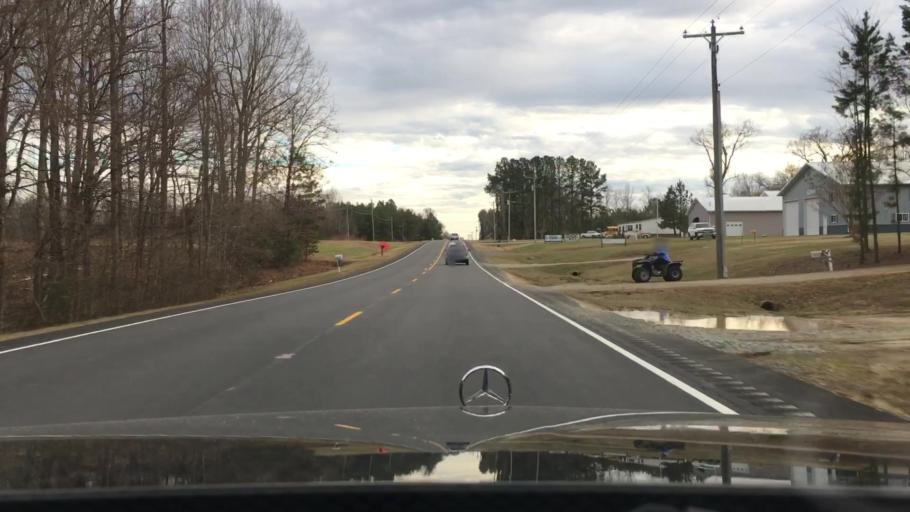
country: US
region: North Carolina
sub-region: Alamance County
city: Mebane
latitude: 36.2555
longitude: -79.1928
